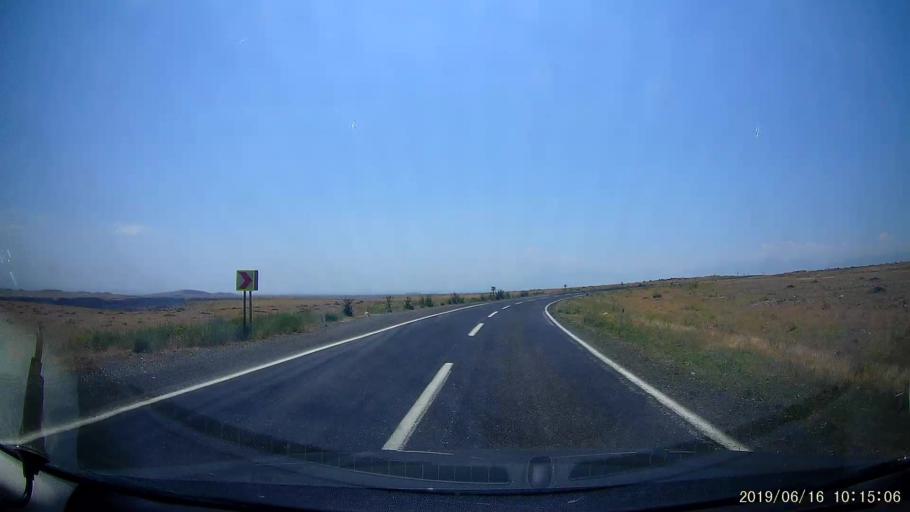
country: TR
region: Igdir
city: Tuzluca
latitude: 40.1792
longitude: 43.6759
